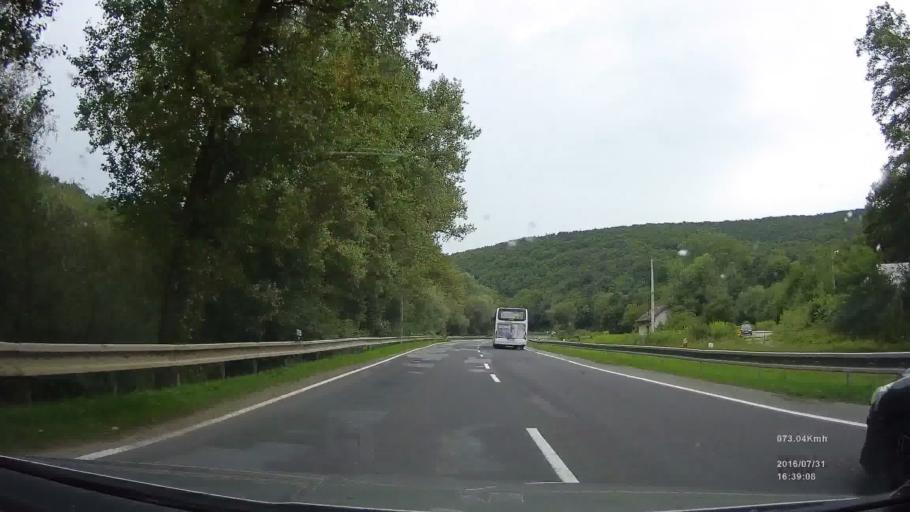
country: SK
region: Presovsky
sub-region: Okres Presov
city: Presov
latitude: 49.1301
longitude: 21.3155
